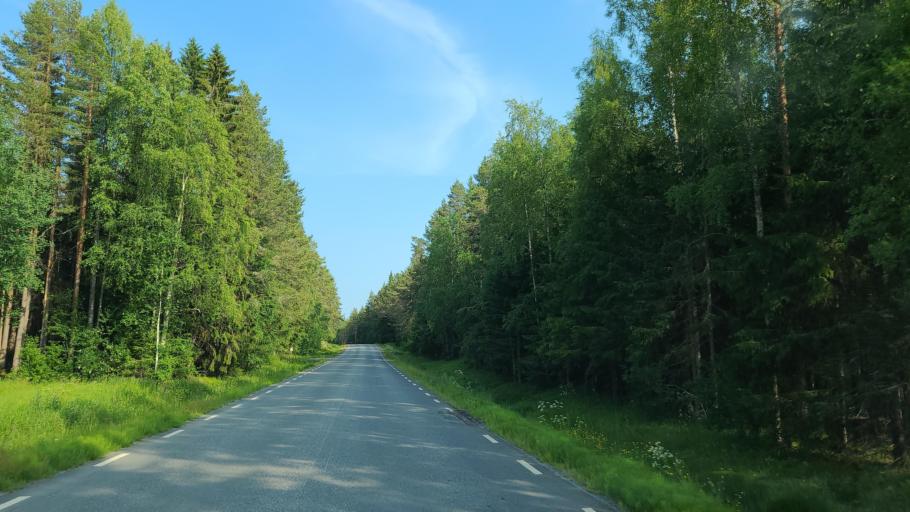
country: SE
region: Vaesterbotten
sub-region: Skelleftea Kommun
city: Burea
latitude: 64.4436
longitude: 21.4860
